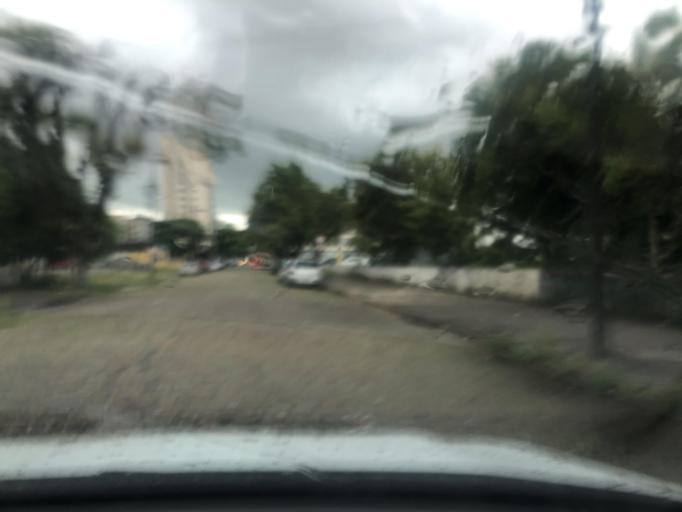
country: BR
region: Santa Catarina
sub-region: Joinville
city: Joinville
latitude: -26.3103
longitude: -48.8441
